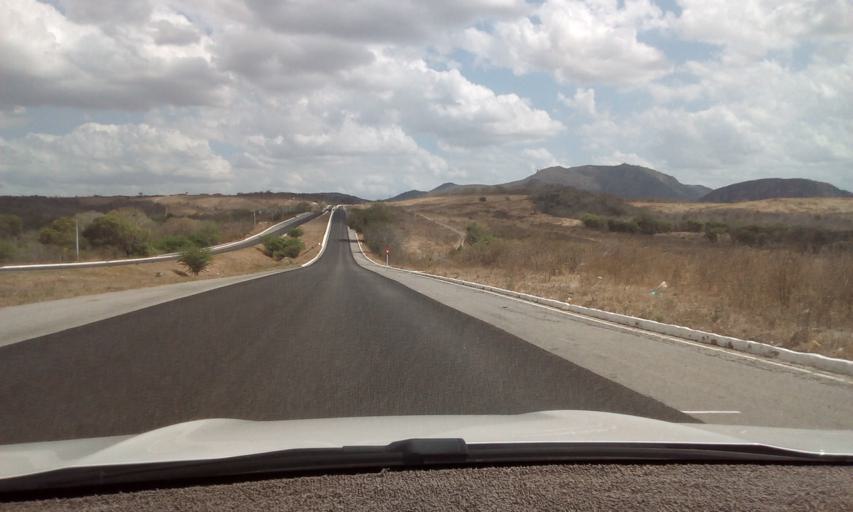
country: BR
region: Pernambuco
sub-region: Toritama
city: Toritama
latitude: -8.0562
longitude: -36.0486
